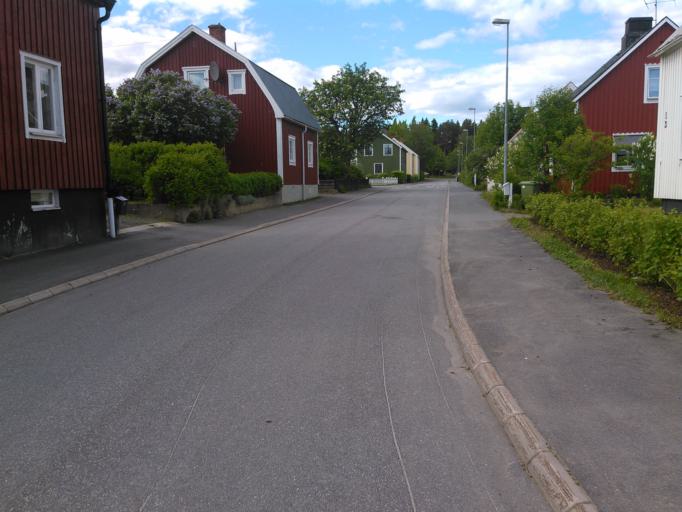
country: SE
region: Vaesterbotten
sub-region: Umea Kommun
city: Umea
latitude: 63.7981
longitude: 20.3105
